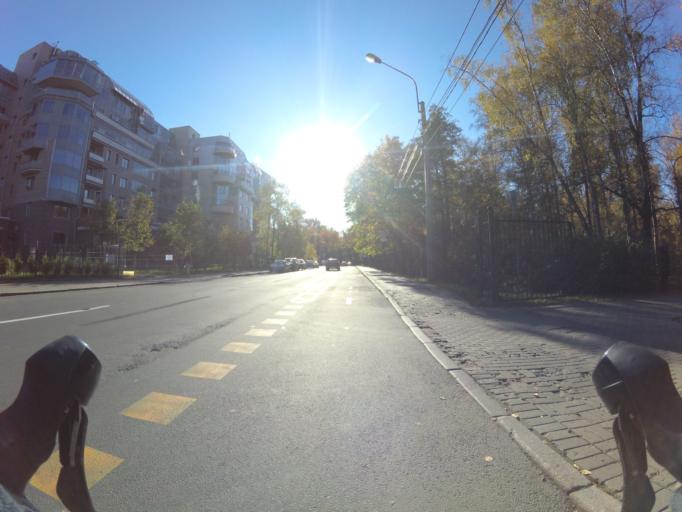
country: RU
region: Leningrad
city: Krestovskiy ostrov
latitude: 59.9702
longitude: 30.2589
